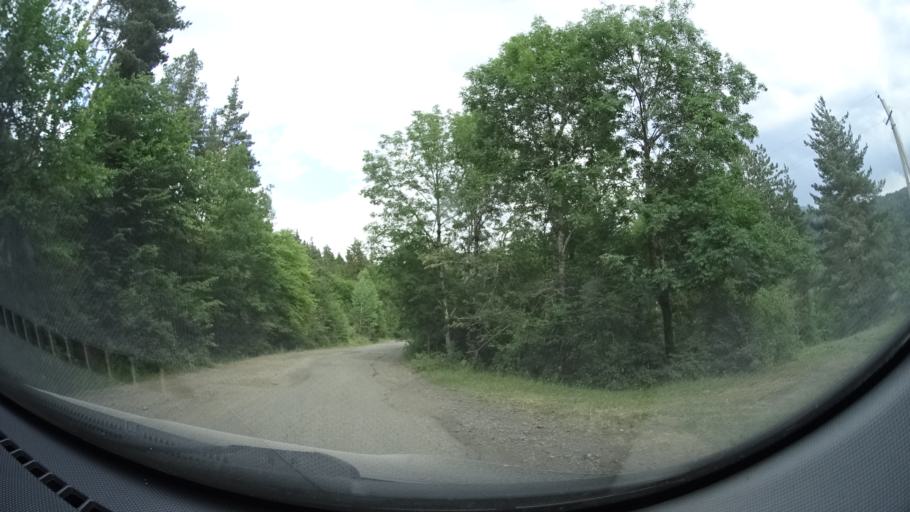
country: GE
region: Samtskhe-Javakheti
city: Adigeni
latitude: 41.6674
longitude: 42.6176
